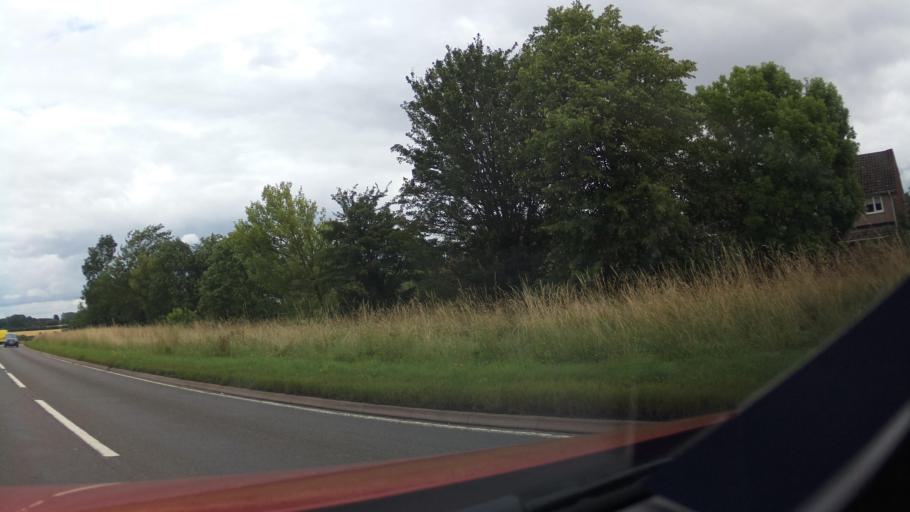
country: GB
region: England
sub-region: Northamptonshire
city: Corby
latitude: 52.4890
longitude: -0.7327
